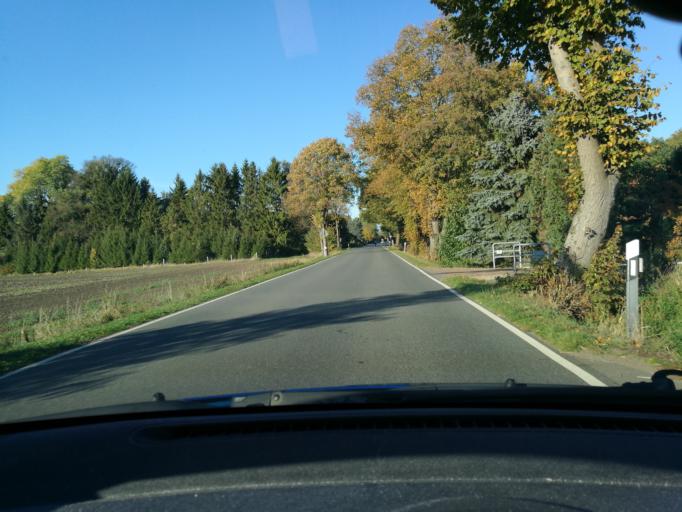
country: DE
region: Lower Saxony
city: Ludersburg
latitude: 53.3168
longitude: 10.5731
